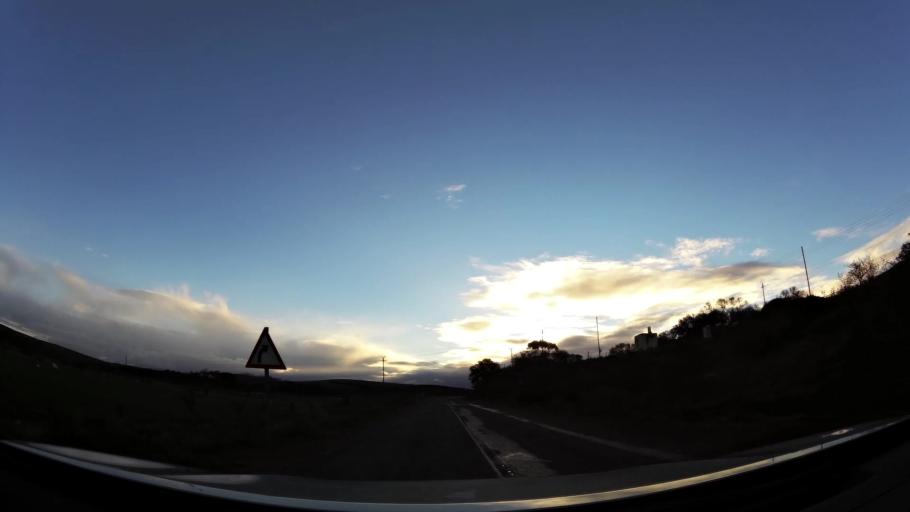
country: ZA
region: Western Cape
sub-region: Eden District Municipality
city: Riversdale
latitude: -34.0744
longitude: 20.9133
